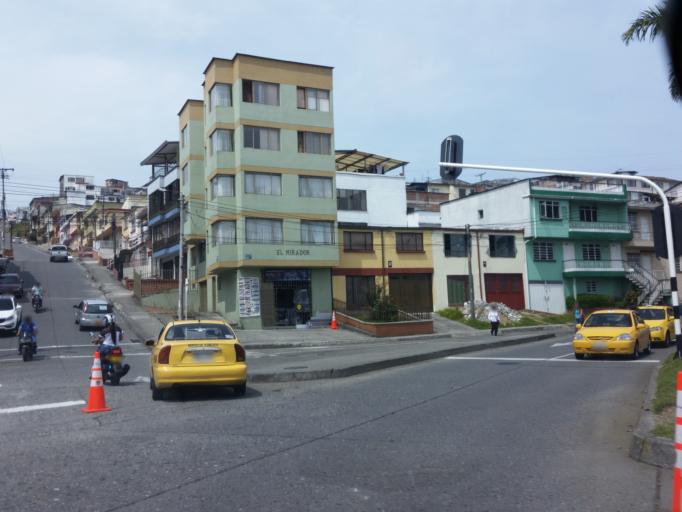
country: CO
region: Caldas
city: Manizales
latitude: 5.0735
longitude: -75.5203
